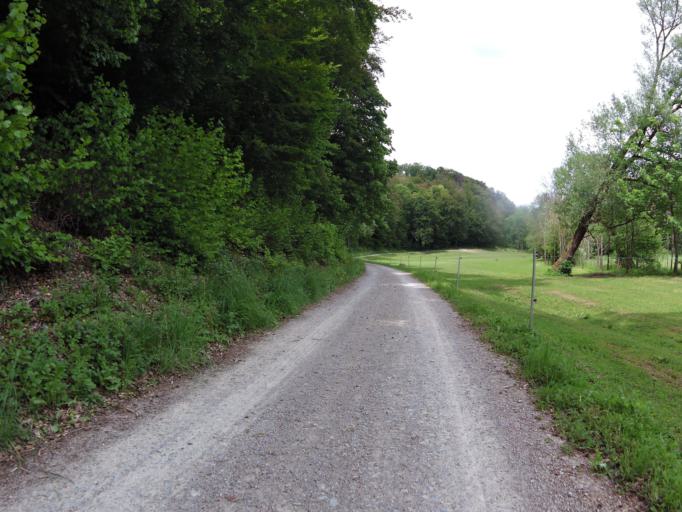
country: DE
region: Thuringia
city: Nazza
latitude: 51.1035
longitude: 10.3313
